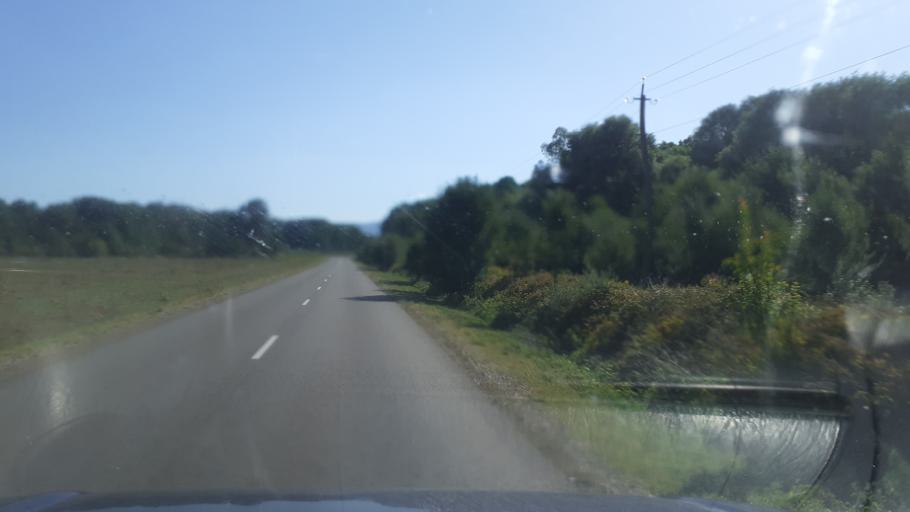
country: RU
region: Krasnodarskiy
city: Azovskaya
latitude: 44.7649
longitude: 38.5676
